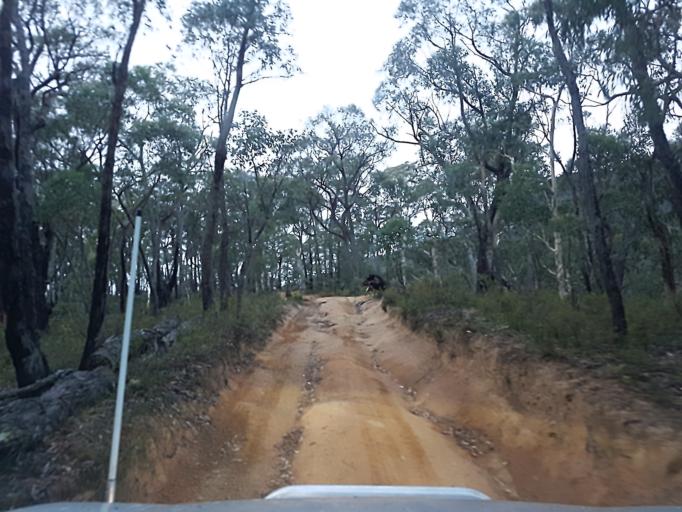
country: AU
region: New South Wales
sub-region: Snowy River
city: Jindabyne
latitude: -36.8643
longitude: 148.2363
